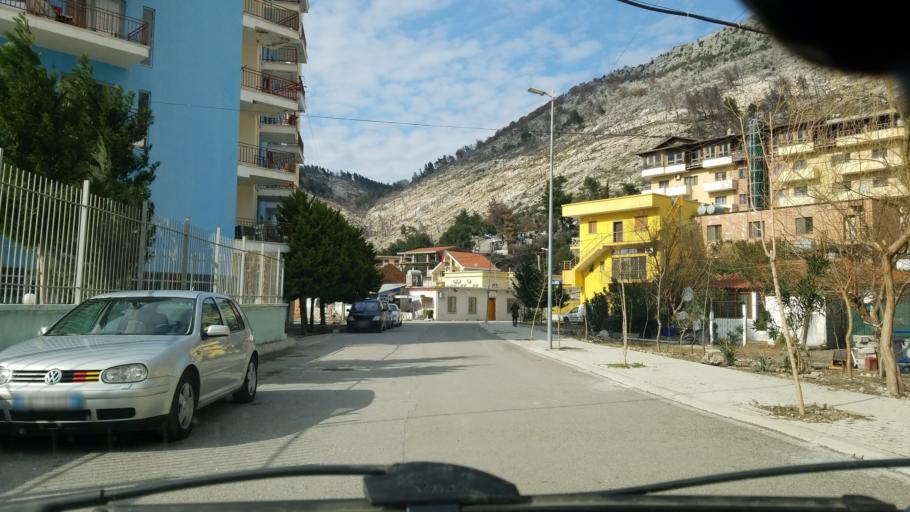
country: AL
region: Lezhe
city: Shengjin
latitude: 41.8139
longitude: 19.5909
